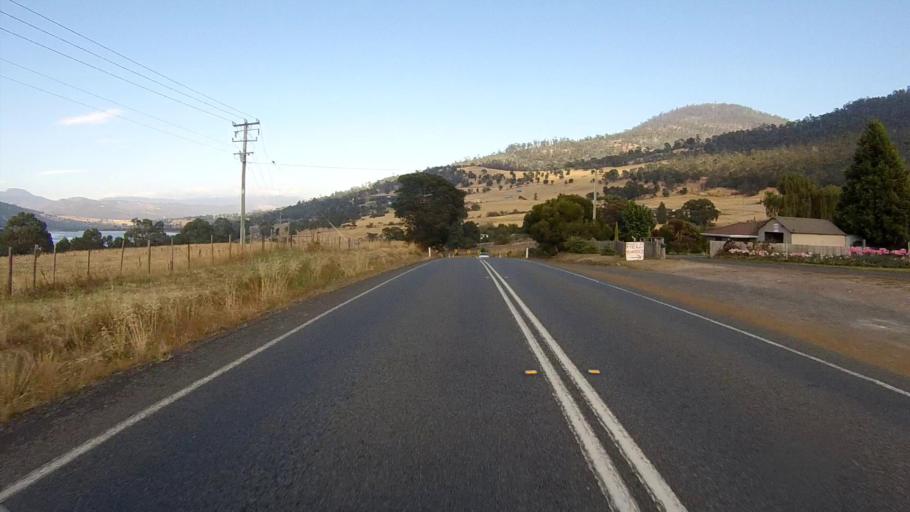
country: AU
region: Tasmania
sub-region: Glenorchy
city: Granton
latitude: -42.7486
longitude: 147.1556
